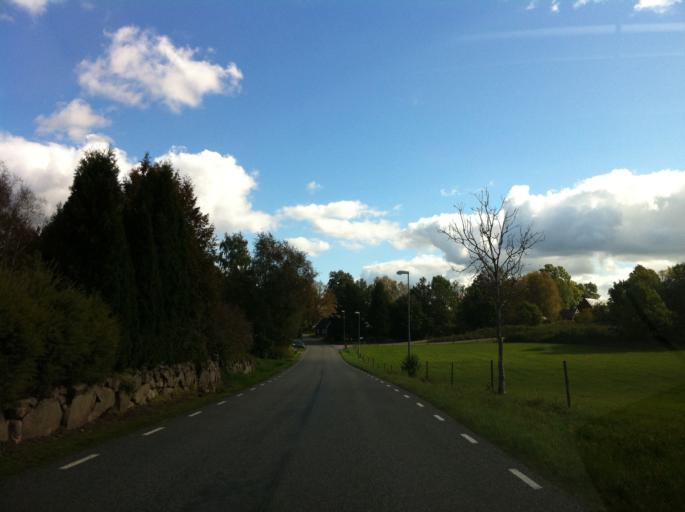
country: SE
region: Skane
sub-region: Kristianstads Kommun
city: Degeberga
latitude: 55.7060
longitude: 13.9985
